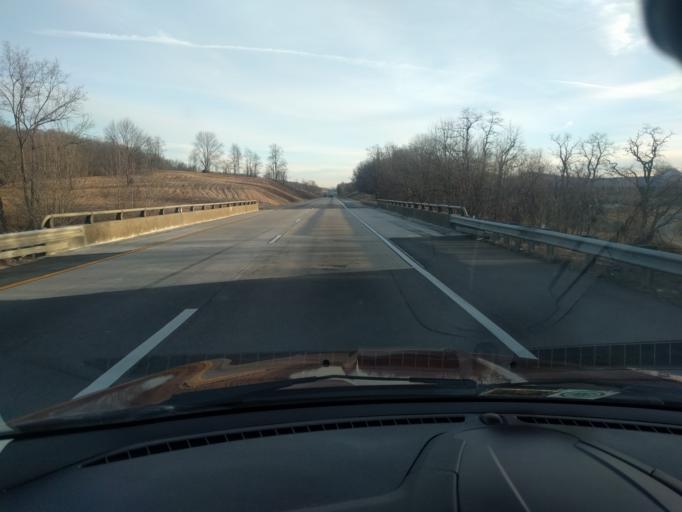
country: US
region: Virginia
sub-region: Augusta County
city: Stuarts Draft
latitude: 38.0099
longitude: -79.1638
